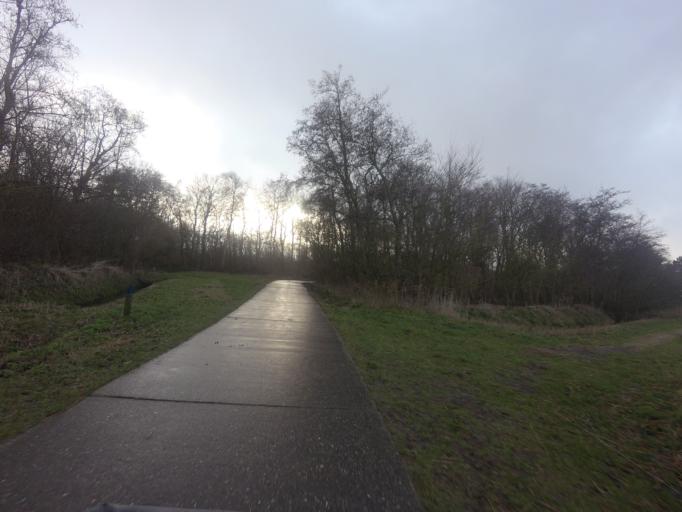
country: NL
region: North Holland
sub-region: Gemeente Texel
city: Den Burg
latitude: 53.1584
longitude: 4.8499
